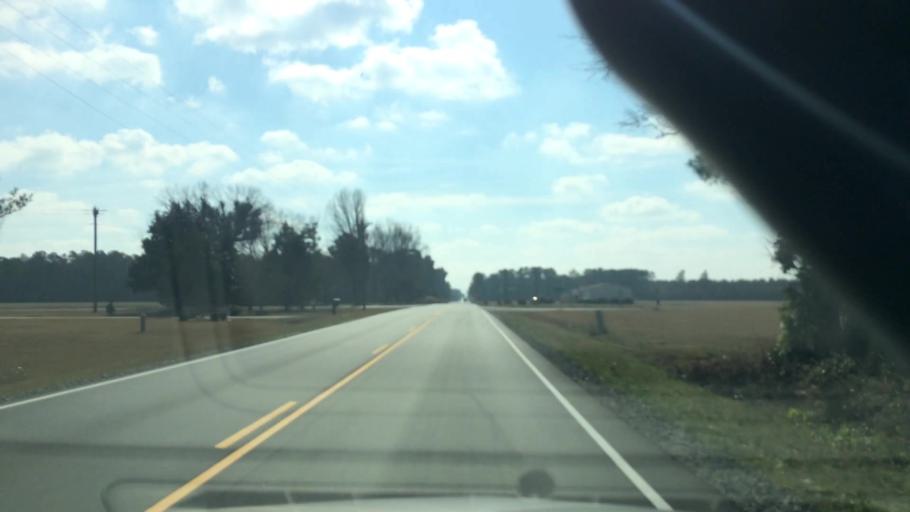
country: US
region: North Carolina
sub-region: Duplin County
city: Beulaville
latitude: 35.0304
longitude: -77.7480
